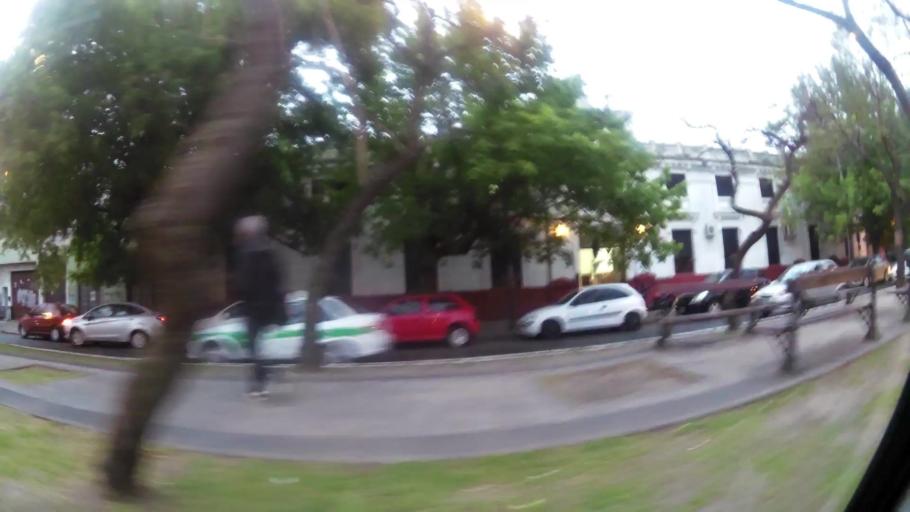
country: AR
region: Buenos Aires
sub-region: Partido de La Plata
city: La Plata
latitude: -34.9218
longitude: -57.9619
